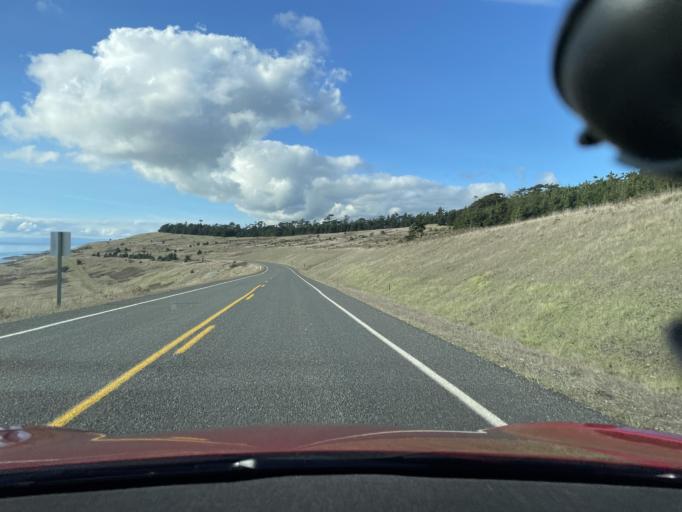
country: US
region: Washington
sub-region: San Juan County
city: Friday Harbor
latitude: 48.4559
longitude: -122.9781
